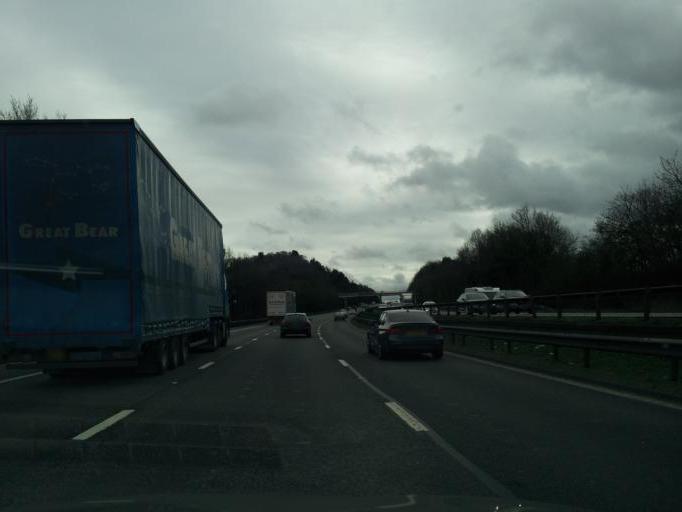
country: GB
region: England
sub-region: Staffordshire
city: Newcastle under Lyme
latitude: 52.9675
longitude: -2.2221
